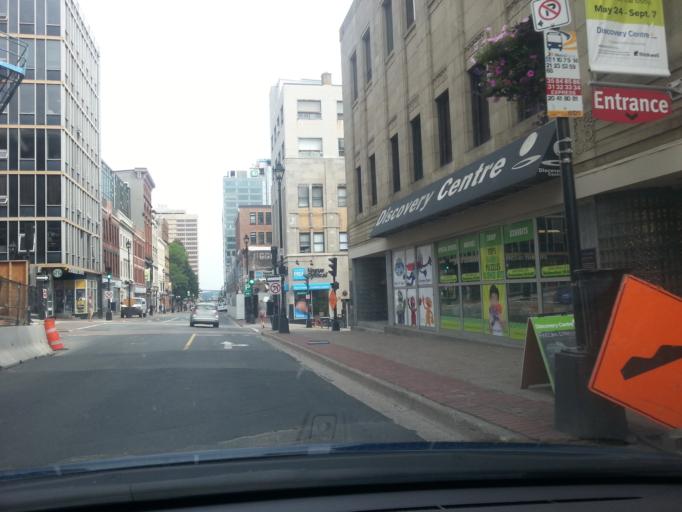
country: CA
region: Nova Scotia
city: Halifax
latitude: 44.6459
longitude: -63.5734
